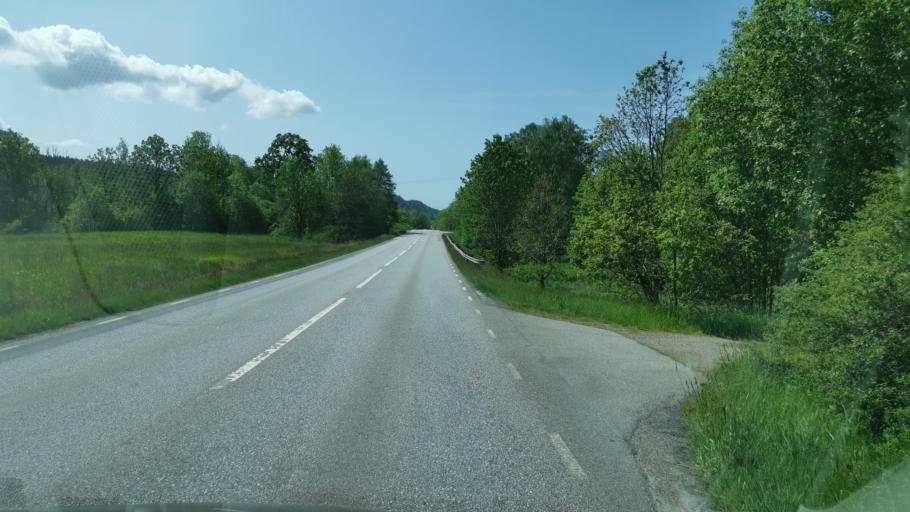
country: SE
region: Vaestra Goetaland
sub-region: Orust
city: Henan
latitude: 58.3353
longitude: 11.6473
